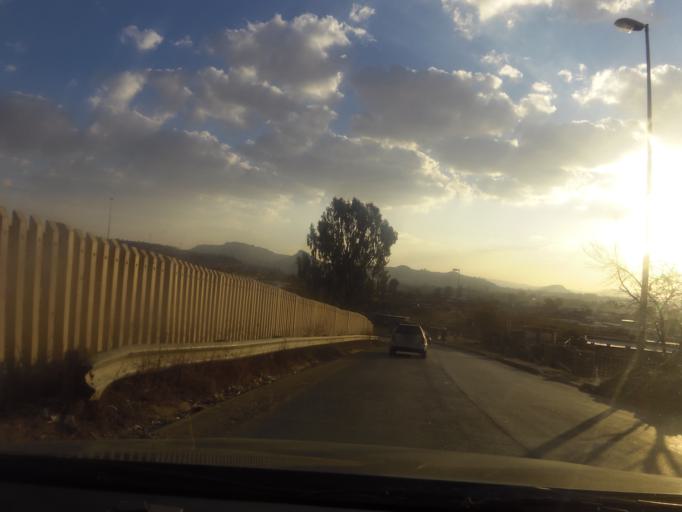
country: LS
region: Maseru
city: Maseru
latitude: -29.3142
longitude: 27.5377
